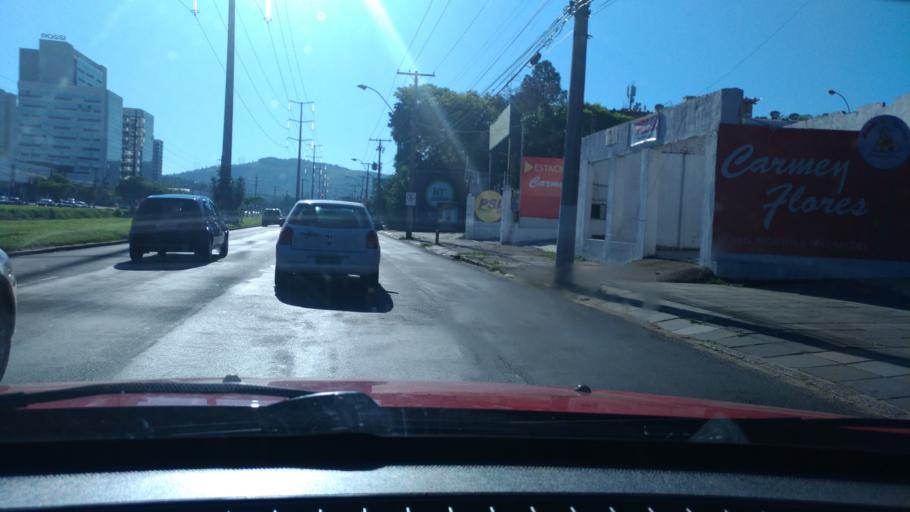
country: BR
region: Rio Grande do Sul
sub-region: Porto Alegre
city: Porto Alegre
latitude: -30.0560
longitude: -51.1667
